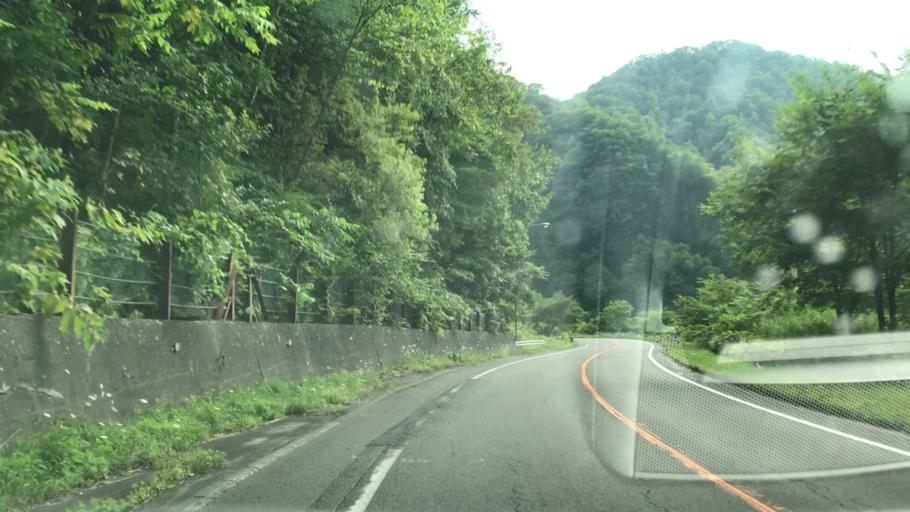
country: JP
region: Hokkaido
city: Shizunai-furukawacho
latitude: 42.7950
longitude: 142.3945
